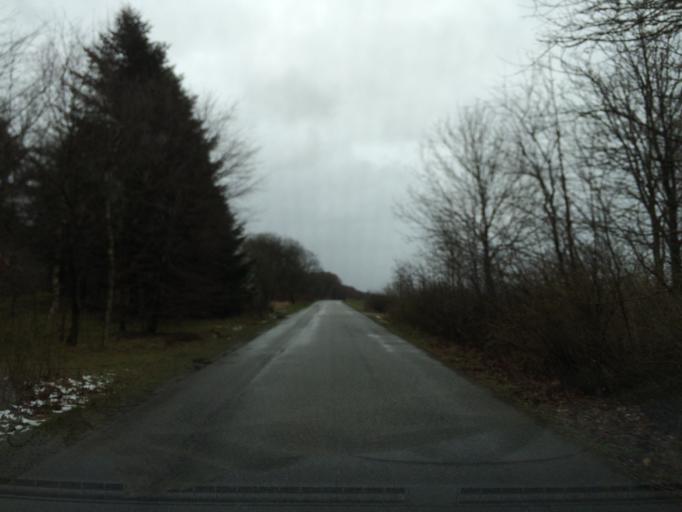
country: DK
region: Central Jutland
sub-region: Ringkobing-Skjern Kommune
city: Videbaek
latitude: 56.2070
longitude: 8.5462
